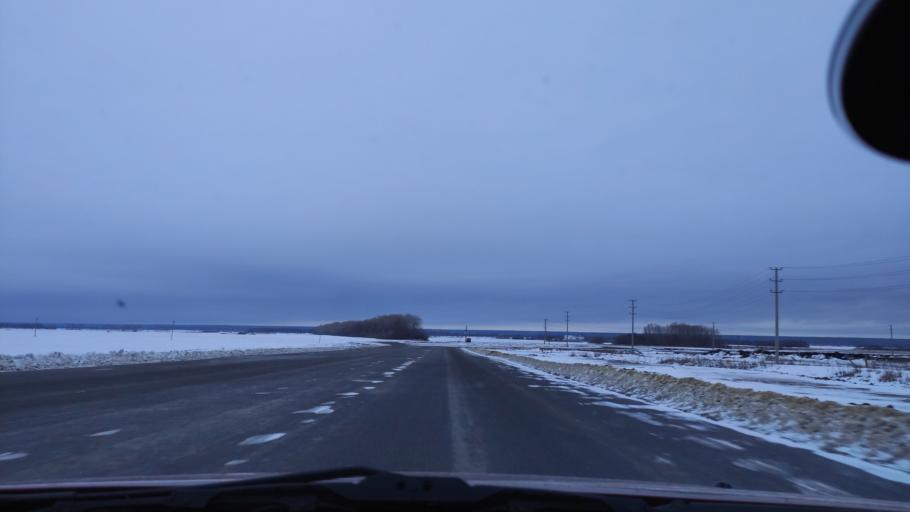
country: RU
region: Tambov
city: Donskoye
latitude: 52.7873
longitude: 41.4311
